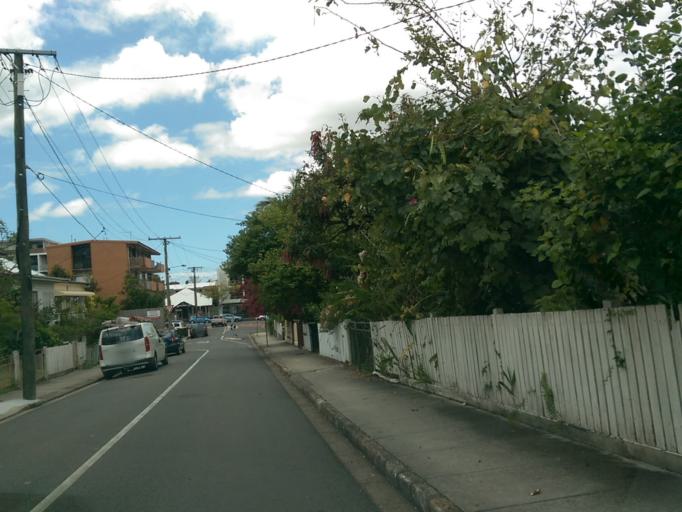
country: AU
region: Queensland
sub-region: Brisbane
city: Fortitude Valley
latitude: -27.4635
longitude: 153.0397
